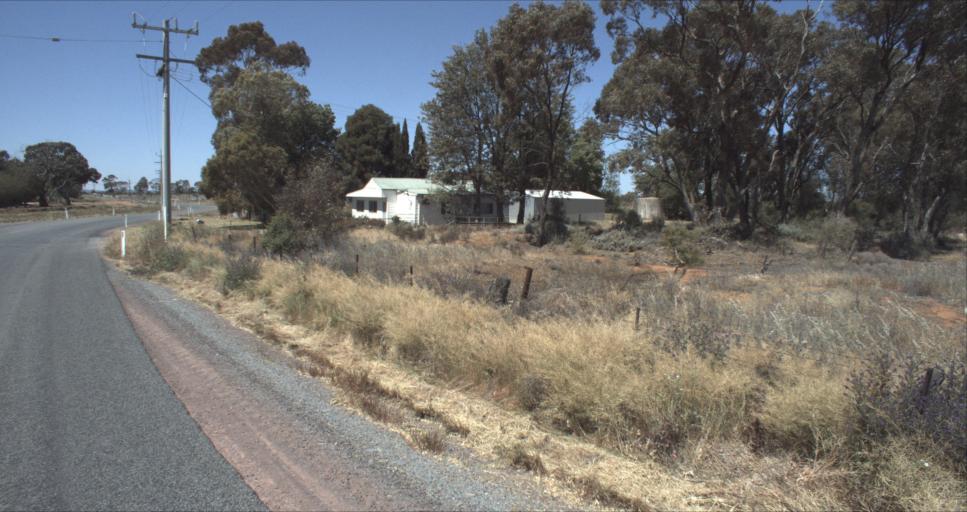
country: AU
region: New South Wales
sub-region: Leeton
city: Leeton
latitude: -34.5285
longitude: 146.4030
